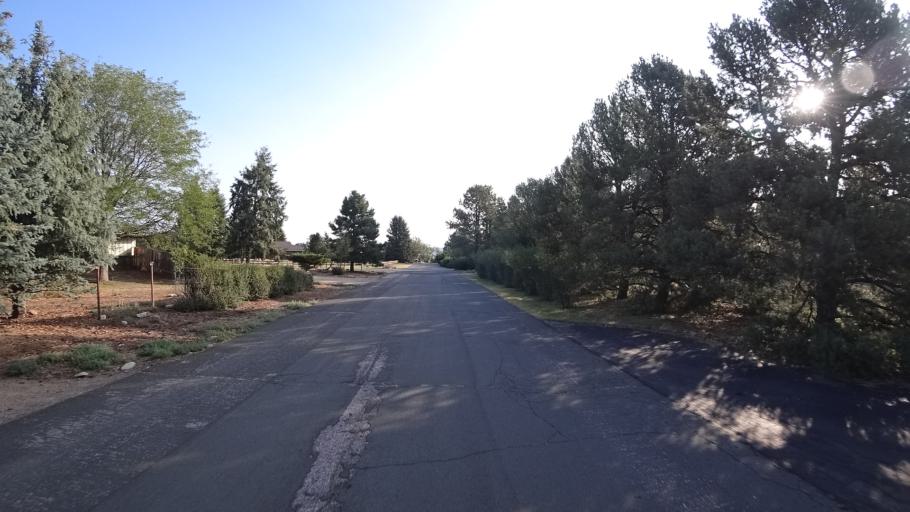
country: US
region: Colorado
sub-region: El Paso County
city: Colorado Springs
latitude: 38.8088
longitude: -104.8554
